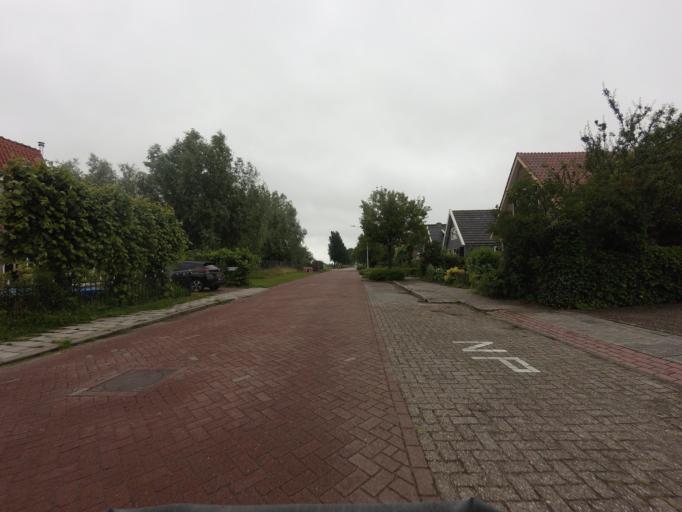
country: NL
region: North Holland
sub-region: Gemeente Schagen
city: Schagen
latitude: 52.7698
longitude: 4.8824
